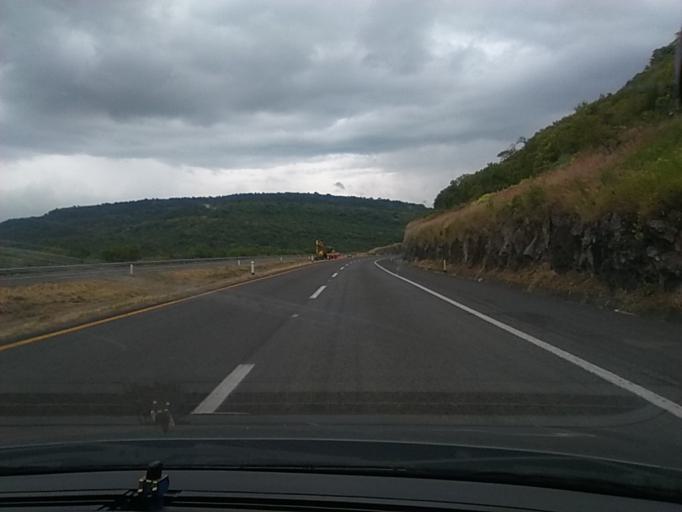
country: MX
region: Jalisco
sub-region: Zapotlan del Rey
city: Zapotlan del Rey
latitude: 20.4989
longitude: -102.9490
